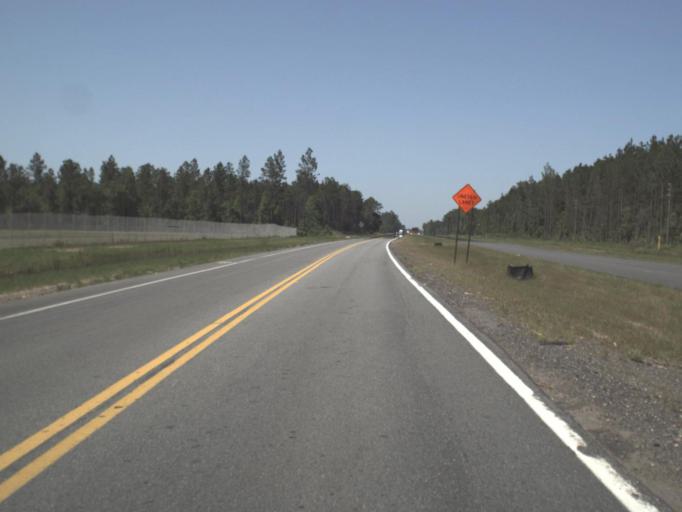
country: US
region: Florida
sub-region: Duval County
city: Baldwin
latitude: 30.3344
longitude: -81.9573
